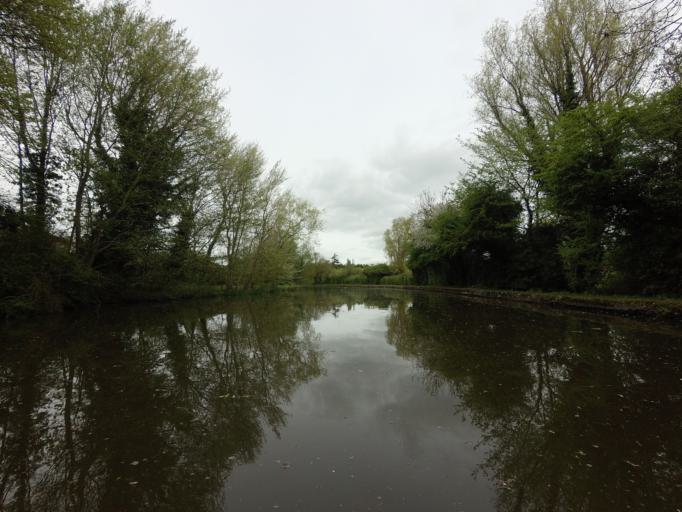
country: GB
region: England
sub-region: Milton Keynes
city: Simpson
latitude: 52.0235
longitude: -0.7237
